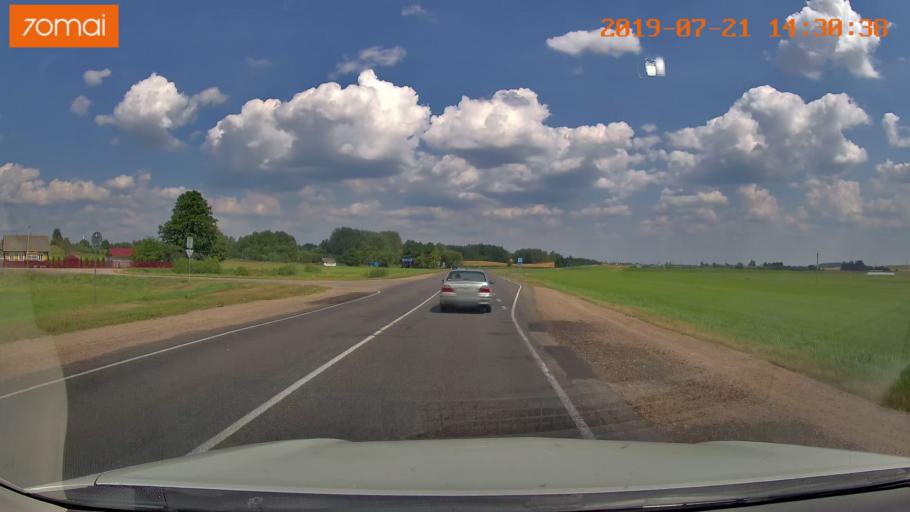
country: BY
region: Grodnenskaya
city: Karelichy
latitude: 53.5245
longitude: 26.2763
